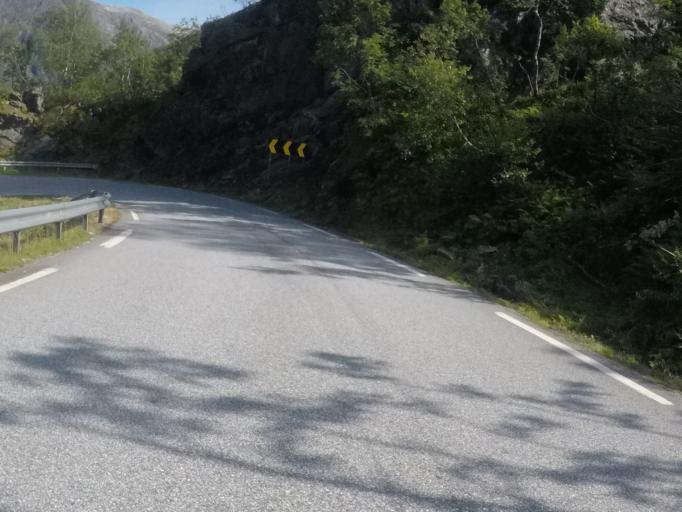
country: NO
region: Sogn og Fjordane
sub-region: Balestrand
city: Balestrand
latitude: 61.3533
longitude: 6.5265
